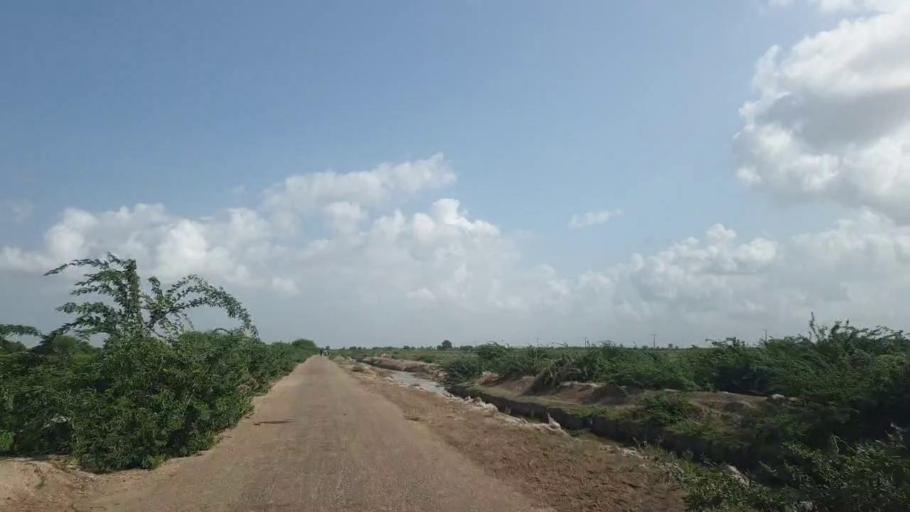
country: PK
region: Sindh
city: Kadhan
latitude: 24.5735
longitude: 69.0671
